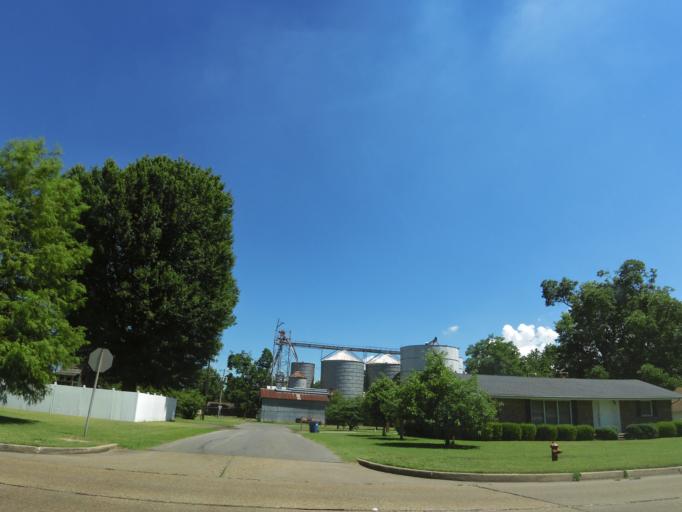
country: US
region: Missouri
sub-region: New Madrid County
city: New Madrid
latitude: 36.5886
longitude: -89.5302
